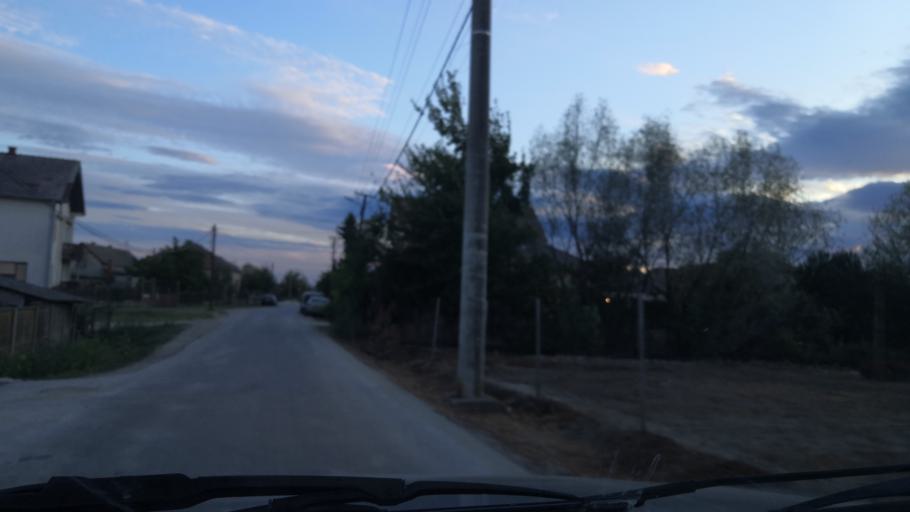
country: RO
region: Mehedinti
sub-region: Comuna Gogosu
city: Balta Verde
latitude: 44.2920
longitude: 22.5819
